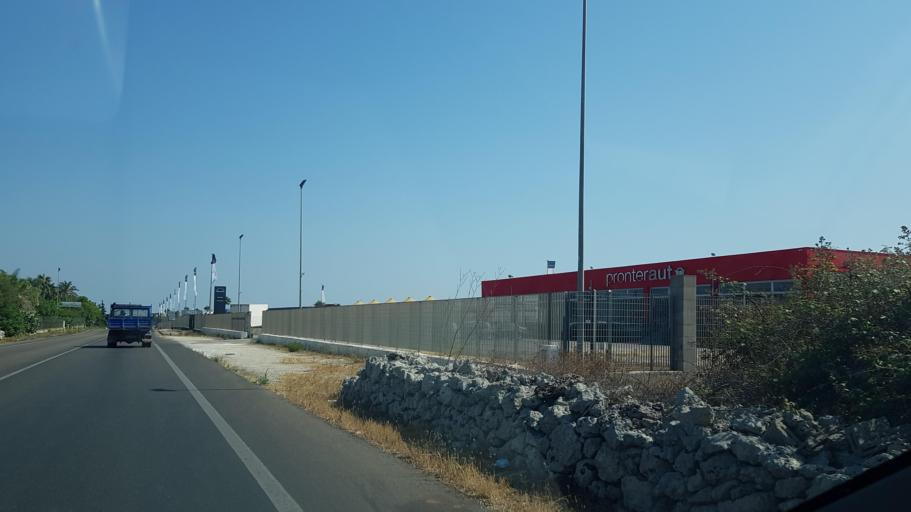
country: IT
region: Apulia
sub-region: Provincia di Lecce
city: Nociglia
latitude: 40.0194
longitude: 18.3245
